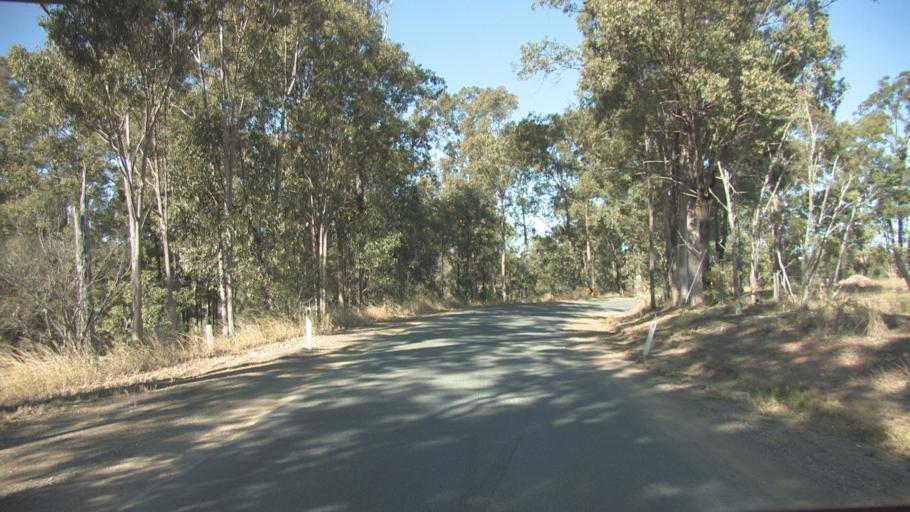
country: AU
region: Queensland
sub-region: Logan
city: Cedar Vale
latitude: -27.8920
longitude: 153.0180
